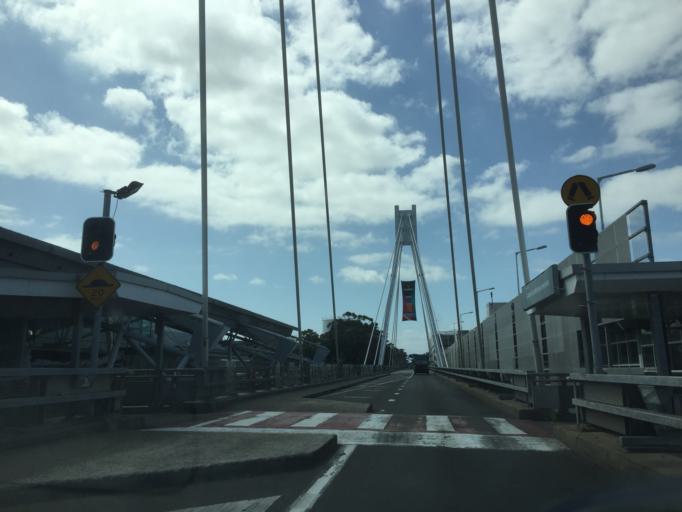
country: AU
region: New South Wales
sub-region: Botany Bay
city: Mascot
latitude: -33.9329
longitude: 151.1793
